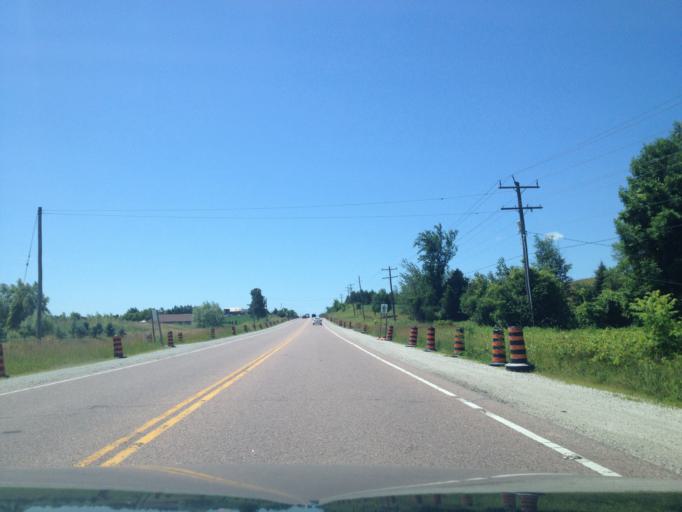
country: CA
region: Ontario
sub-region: Halton
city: Milton
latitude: 43.6658
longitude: -79.9968
